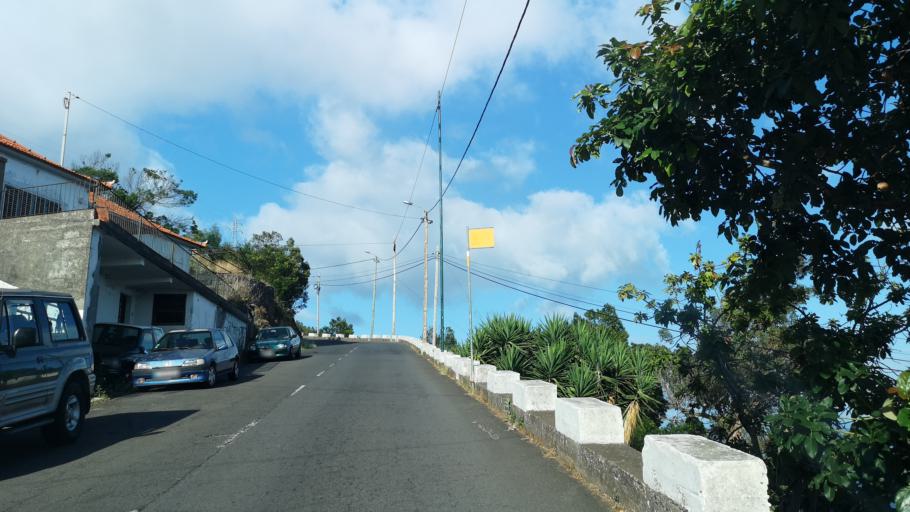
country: PT
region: Madeira
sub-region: Santa Cruz
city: Camacha
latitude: 32.6585
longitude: -16.8365
